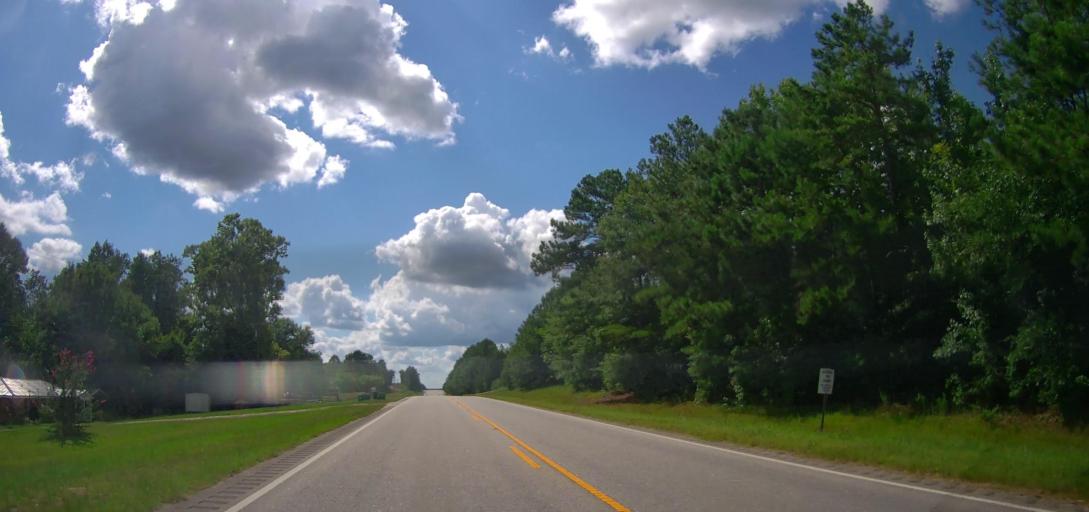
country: US
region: Alabama
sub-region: Macon County
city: Tuskegee
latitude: 32.4650
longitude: -85.5673
